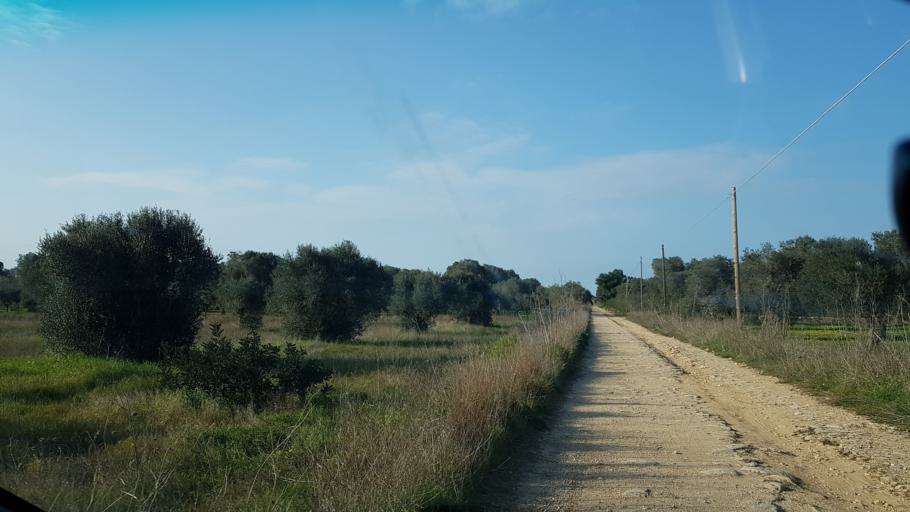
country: IT
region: Apulia
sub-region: Provincia di Brindisi
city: San Vito dei Normanni
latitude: 40.6720
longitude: 17.7908
